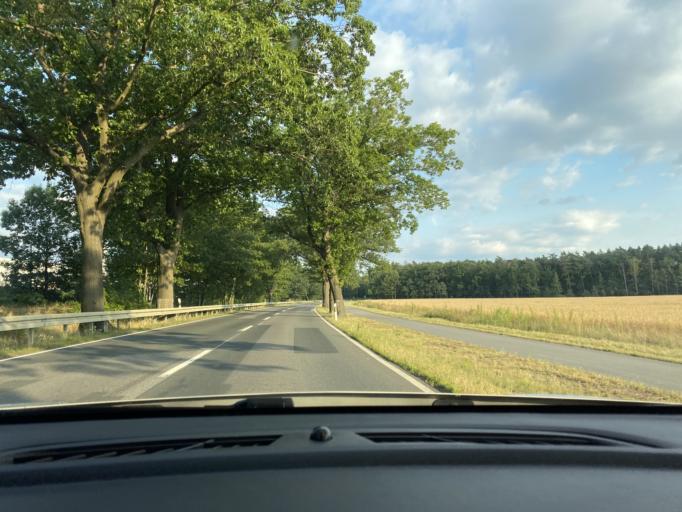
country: DE
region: Saxony
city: Konigswartha
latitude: 51.3433
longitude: 14.3390
